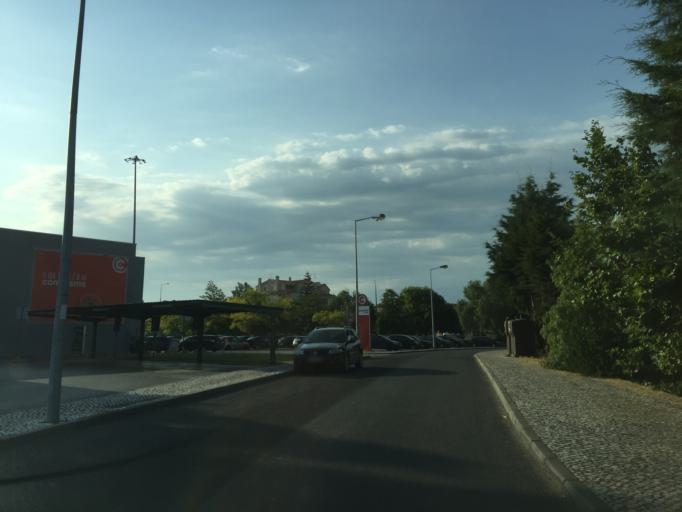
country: PT
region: Santarem
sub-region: Torres Novas
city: Torres Novas
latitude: 39.4728
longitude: -8.5450
